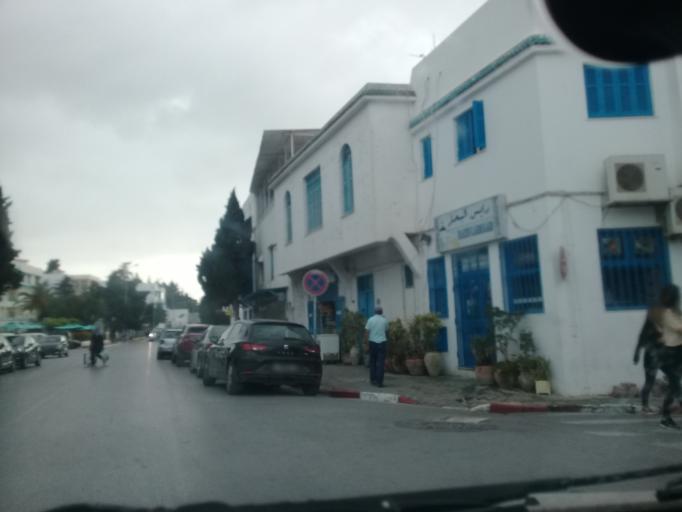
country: TN
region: Tunis
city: Sidi Bou Said
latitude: 36.8697
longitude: 10.3437
